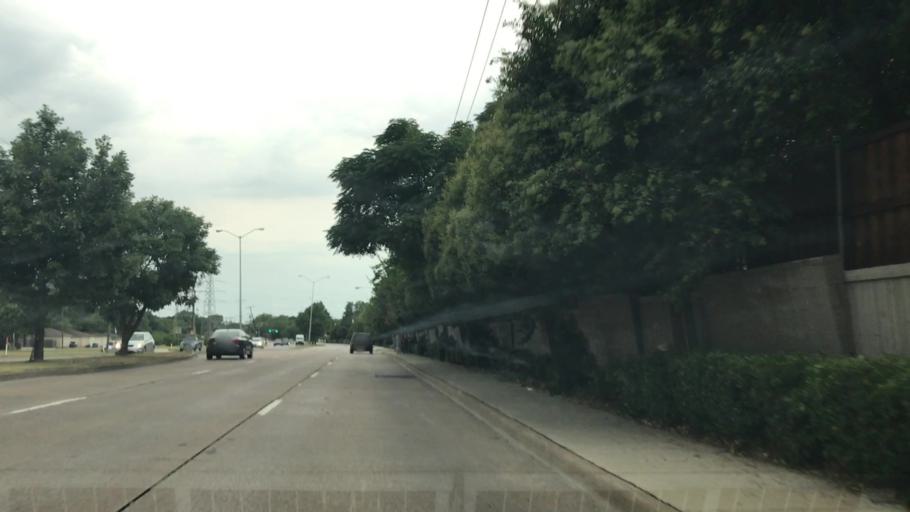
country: US
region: Texas
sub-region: Dallas County
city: Richardson
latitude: 32.9508
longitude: -96.7739
